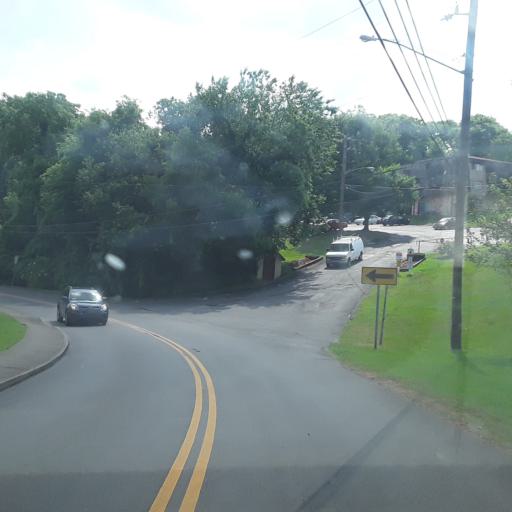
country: US
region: Tennessee
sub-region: Davidson County
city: Oak Hill
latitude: 36.1144
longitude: -86.7361
